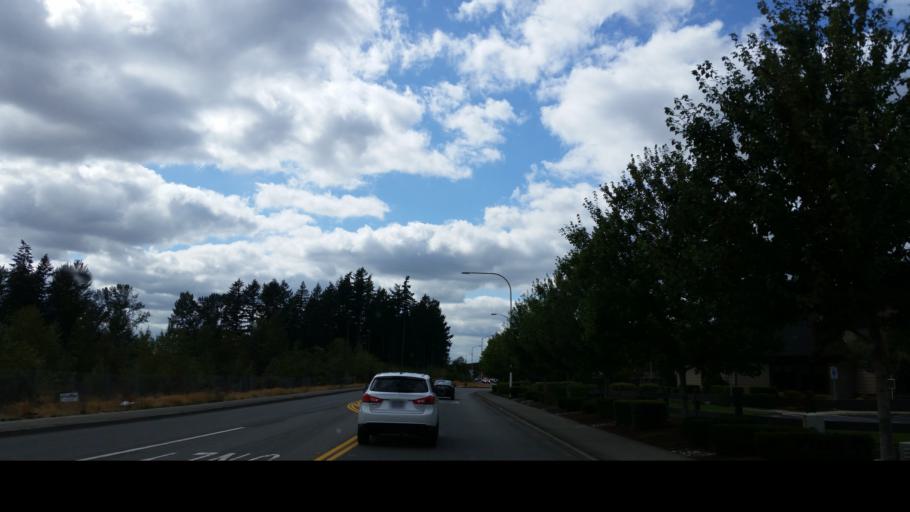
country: US
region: Washington
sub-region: King County
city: Pacific
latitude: 47.2466
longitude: -122.2010
